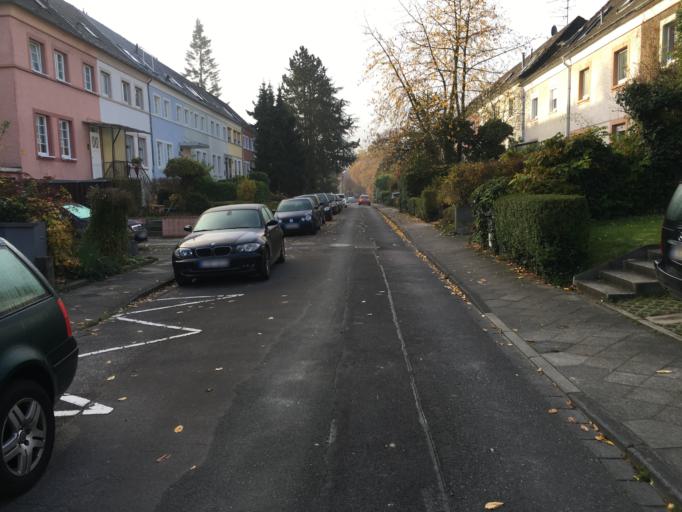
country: DE
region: North Rhine-Westphalia
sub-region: Regierungsbezirk Dusseldorf
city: Ratingen
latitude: 51.2403
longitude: 6.8536
